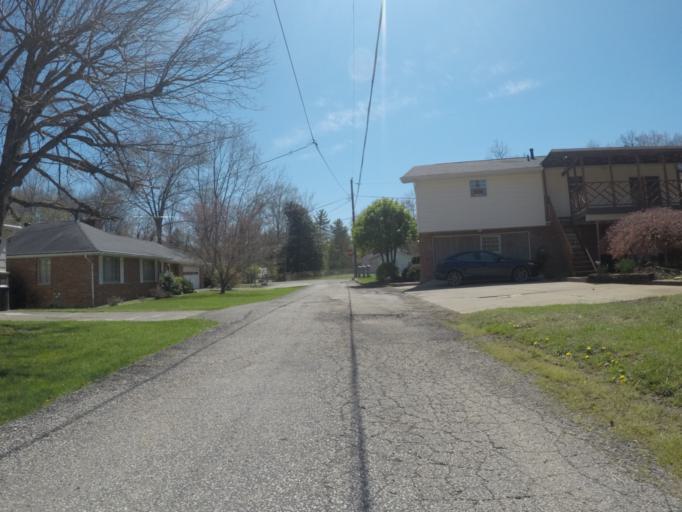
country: US
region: West Virginia
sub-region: Cabell County
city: Pea Ridge
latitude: 38.4212
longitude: -82.3124
